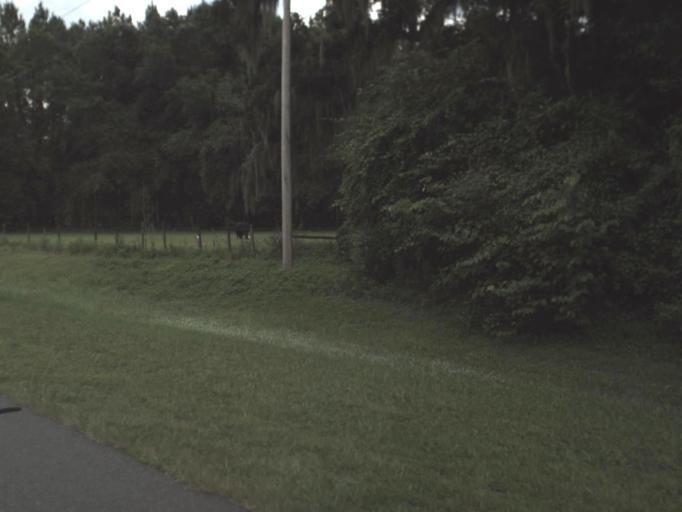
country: US
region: Florida
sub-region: Alachua County
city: Alachua
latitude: 29.8303
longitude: -82.4195
